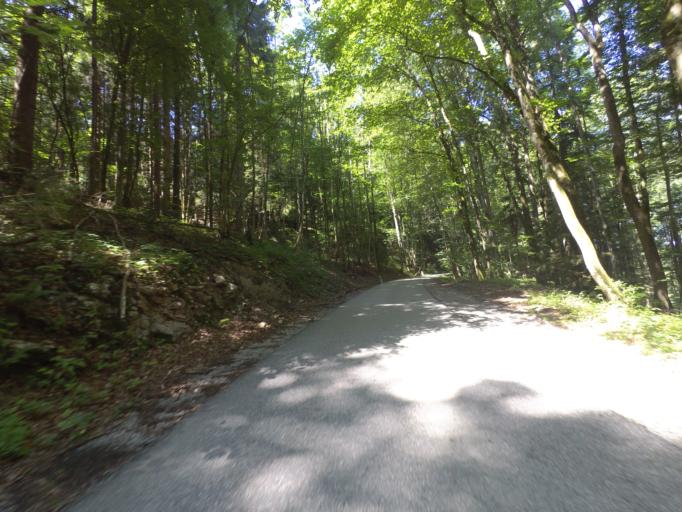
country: AT
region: Salzburg
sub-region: Politischer Bezirk Salzburg-Umgebung
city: Elsbethen
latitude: 47.7650
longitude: 13.1040
